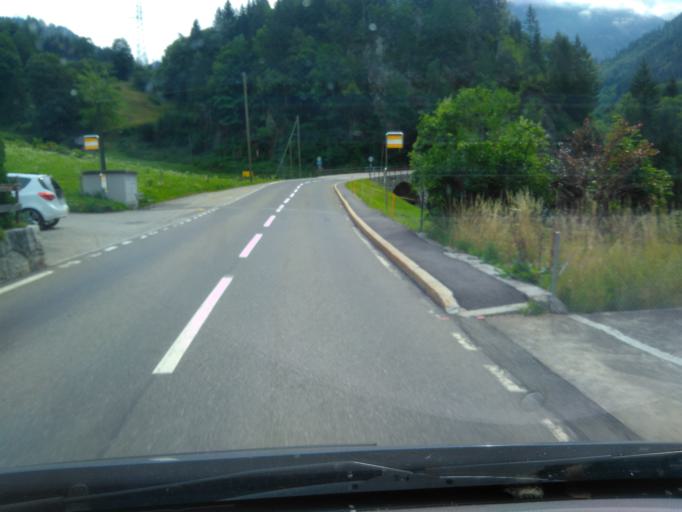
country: CH
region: Bern
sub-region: Interlaken-Oberhasli District
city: Meiringen
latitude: 46.7206
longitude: 8.2968
